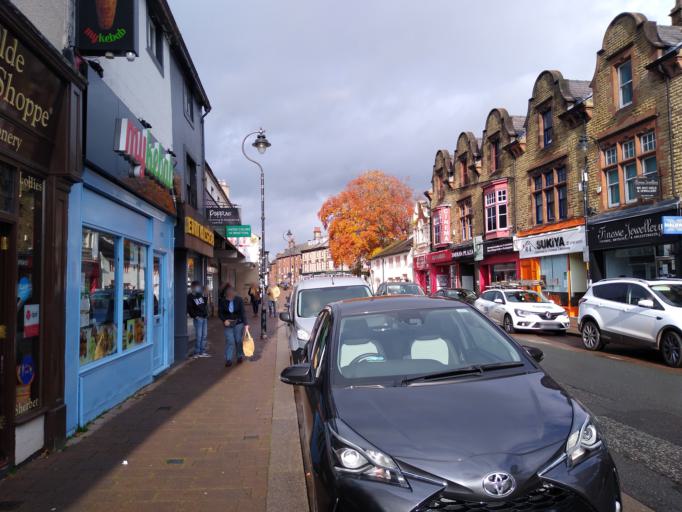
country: GB
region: England
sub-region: Cumbria
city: Penrith
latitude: 54.6653
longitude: -2.7538
